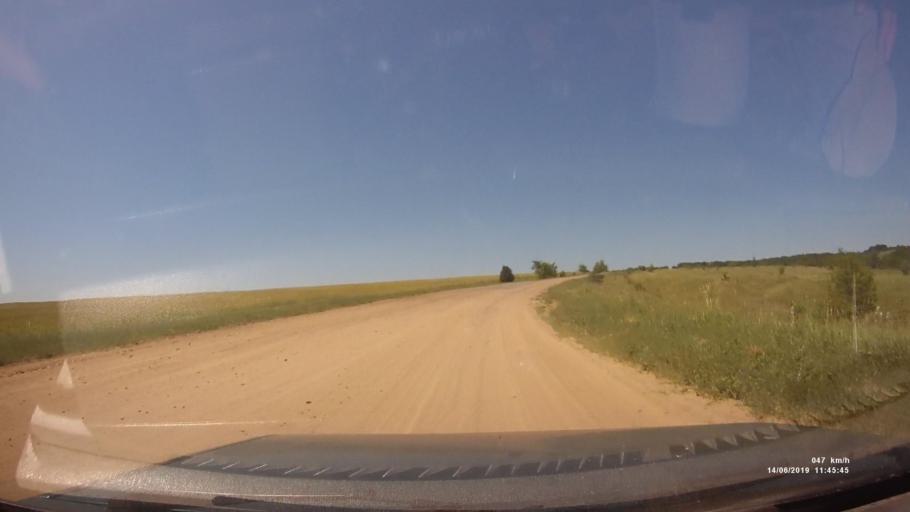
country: RU
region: Rostov
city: Kazanskaya
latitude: 49.8506
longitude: 41.3090
